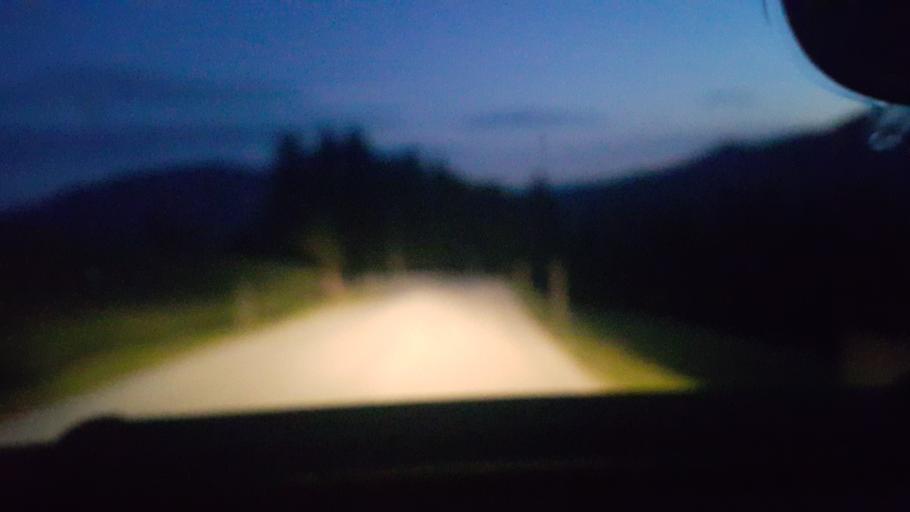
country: SI
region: Vitanje
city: Vitanje
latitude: 46.4143
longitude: 15.2778
